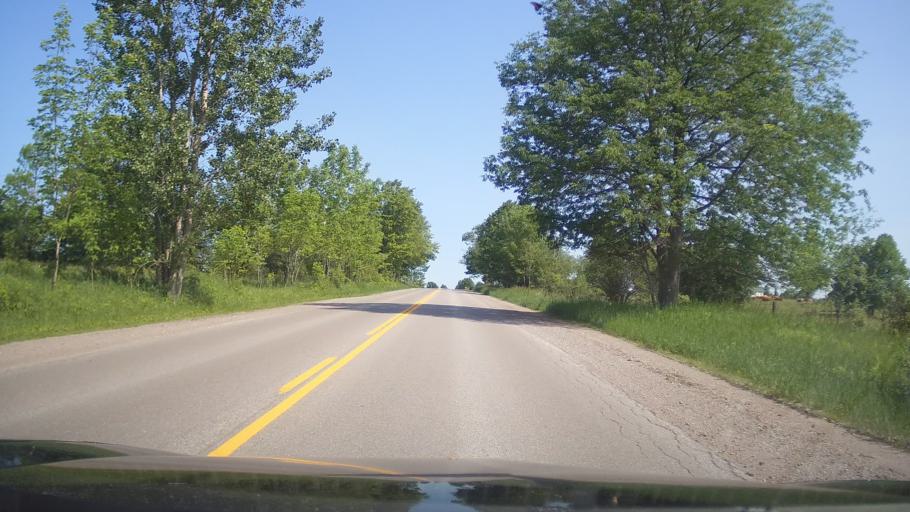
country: CA
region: Ontario
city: Uxbridge
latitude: 44.5286
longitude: -78.9641
